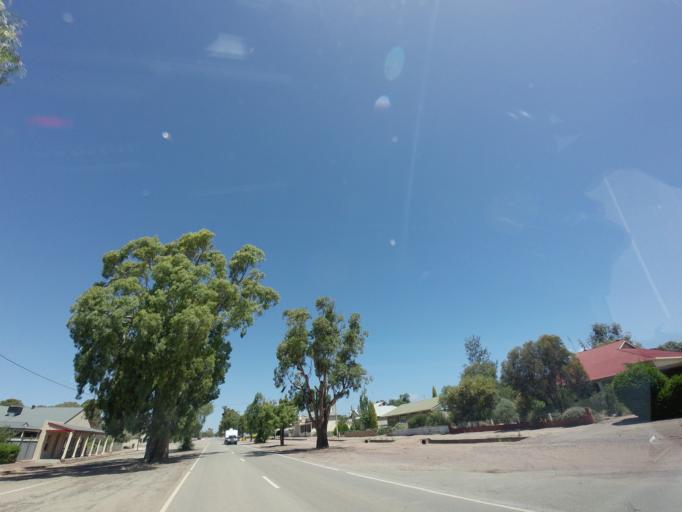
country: AU
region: South Australia
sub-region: Flinders Ranges
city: Quorn
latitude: -32.6492
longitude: 138.0974
